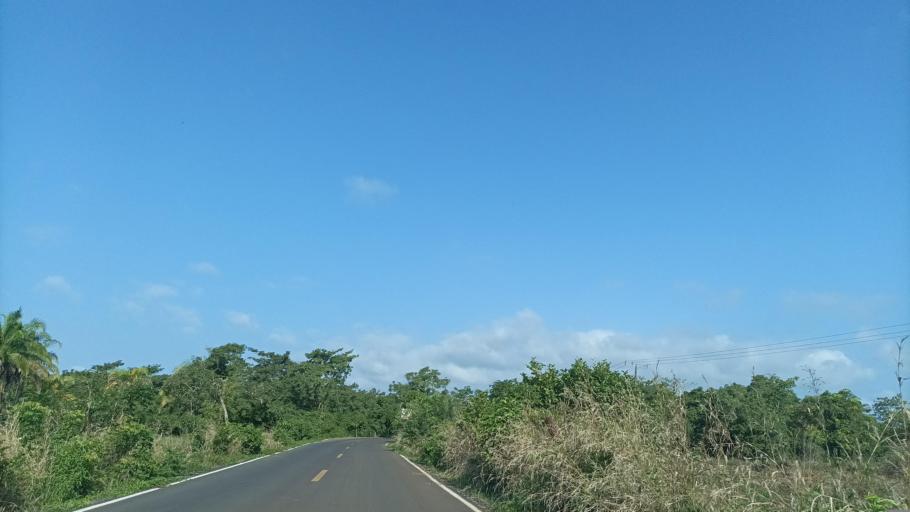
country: MX
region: Veracruz
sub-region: Chinameca
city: Chacalapa
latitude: 18.1399
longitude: -94.6522
